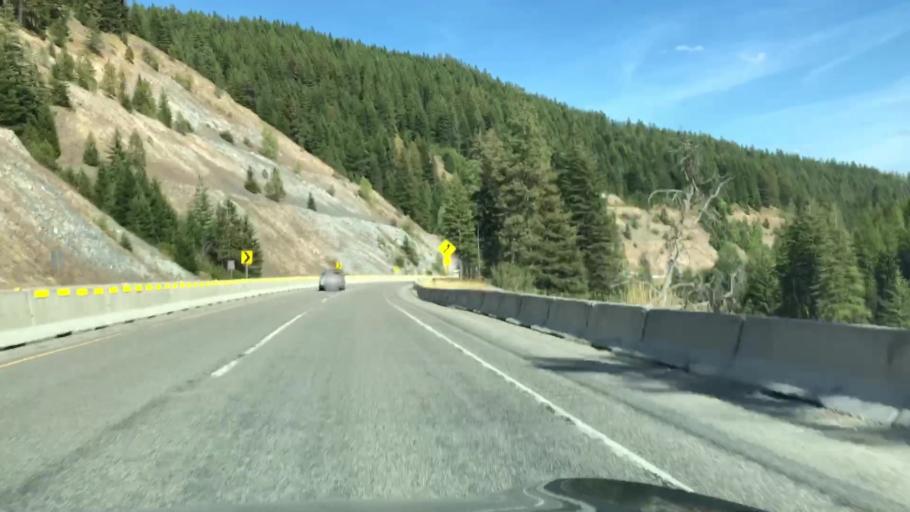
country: US
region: Montana
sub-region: Sanders County
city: Thompson Falls
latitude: 47.4011
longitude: -115.4685
